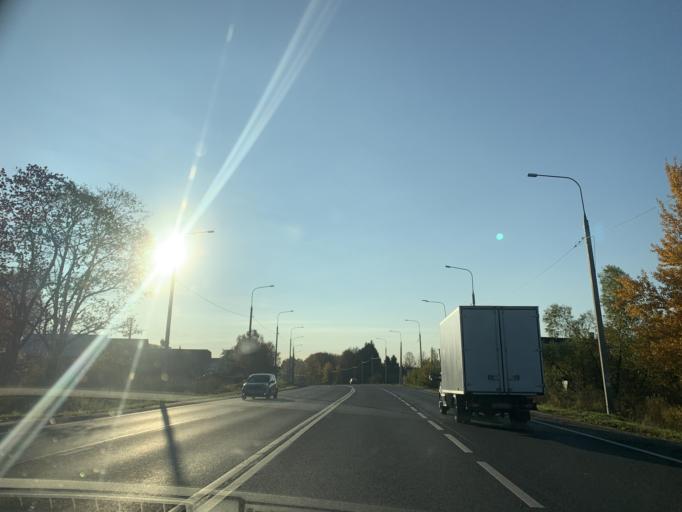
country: RU
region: Jaroslavl
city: Konstantinovskiy
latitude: 57.7696
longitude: 39.6715
